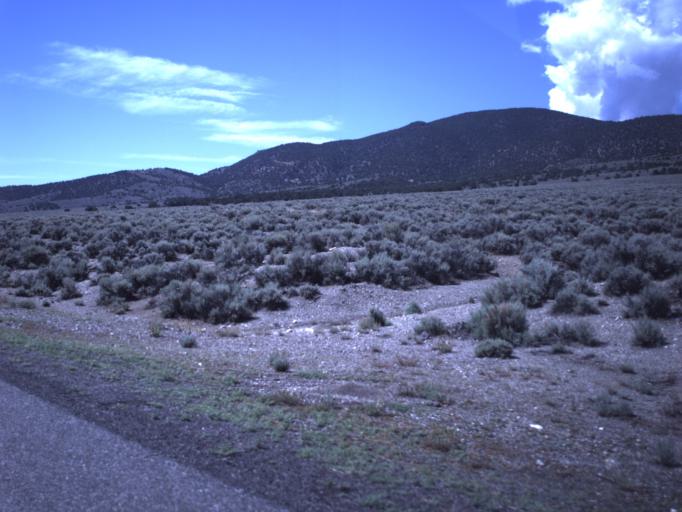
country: US
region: Utah
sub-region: Piute County
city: Junction
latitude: 38.3641
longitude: -112.2237
